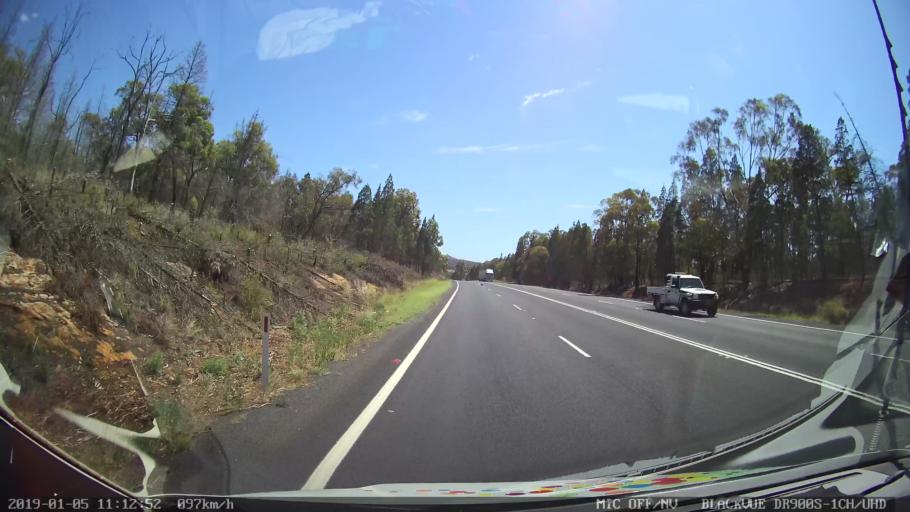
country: AU
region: New South Wales
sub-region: Warrumbungle Shire
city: Coonabarabran
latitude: -31.3774
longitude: 149.2653
